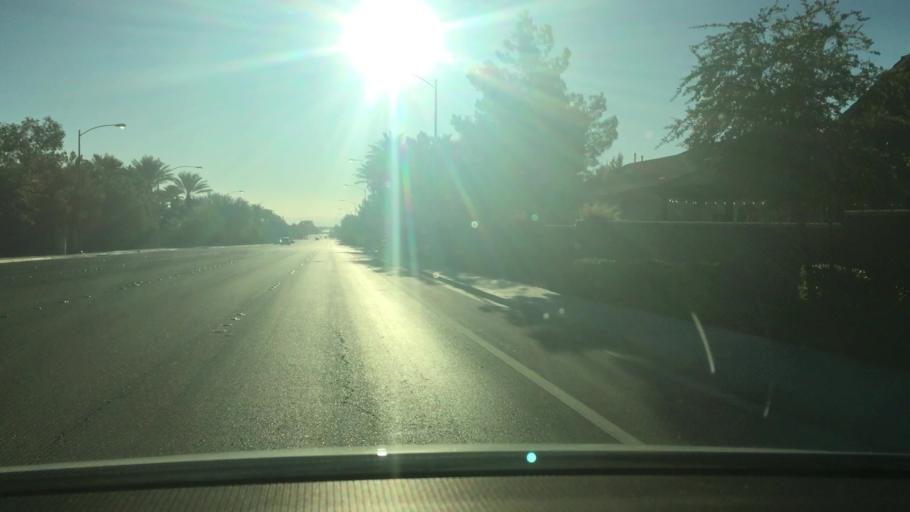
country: US
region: Nevada
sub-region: Clark County
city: Summerlin South
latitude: 36.0775
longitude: -115.3123
